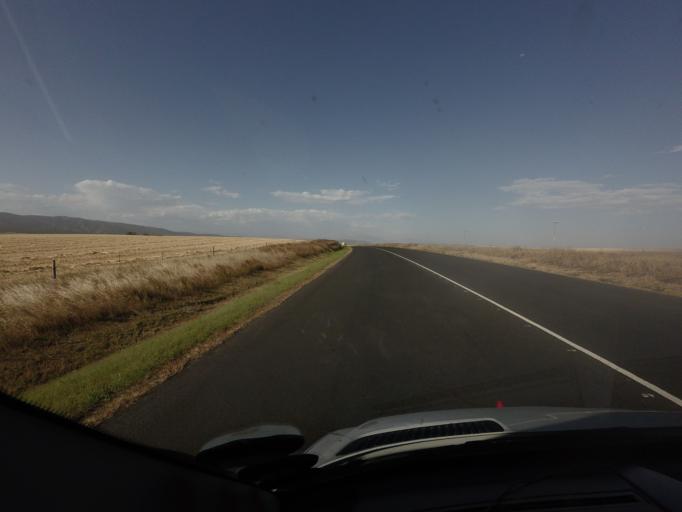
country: ZA
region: Western Cape
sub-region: Cape Winelands District Municipality
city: Ashton
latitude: -34.1392
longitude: 20.0232
